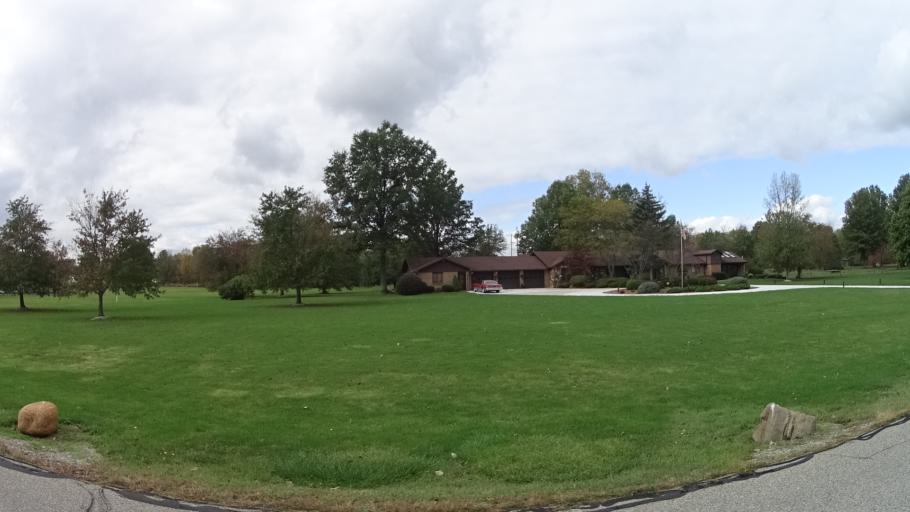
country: US
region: Ohio
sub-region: Lorain County
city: Grafton
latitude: 41.3175
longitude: -82.0544
